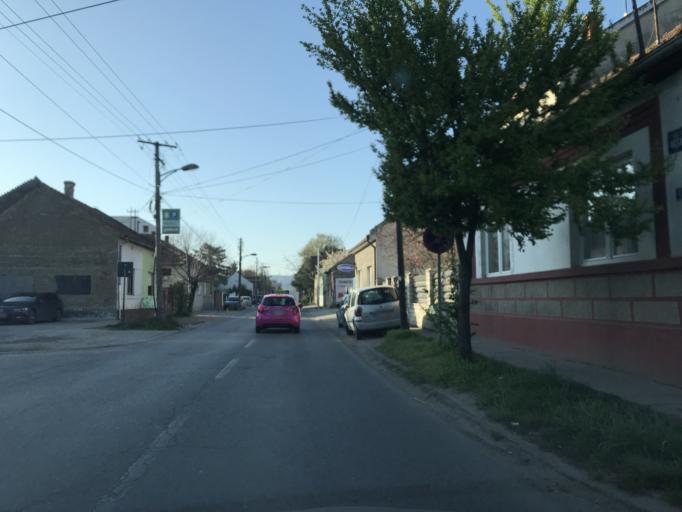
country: RS
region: Autonomna Pokrajina Vojvodina
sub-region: Juznobacki Okrug
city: Novi Sad
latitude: 45.2465
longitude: 19.8082
